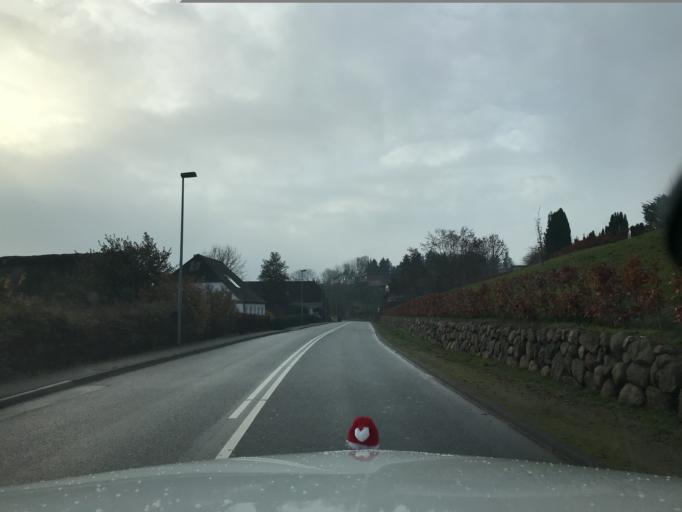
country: DK
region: South Denmark
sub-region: Sonderborg Kommune
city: Grasten
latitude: 54.8967
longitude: 9.5654
